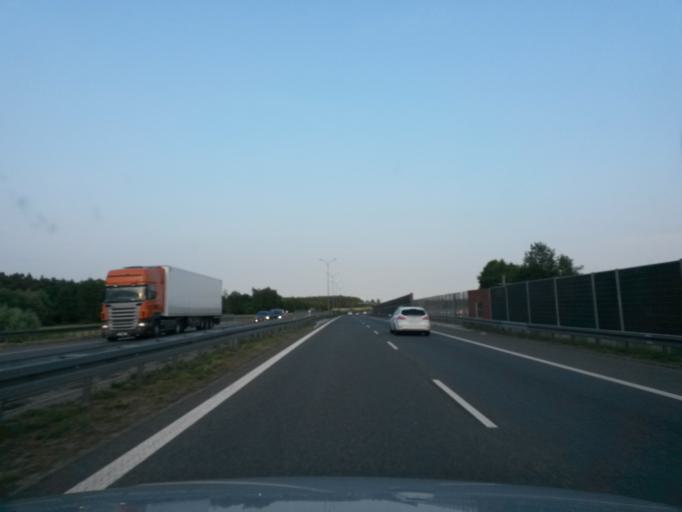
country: PL
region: Lower Silesian Voivodeship
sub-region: Powiat olesnicki
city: Olesnica
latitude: 51.2306
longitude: 17.4261
